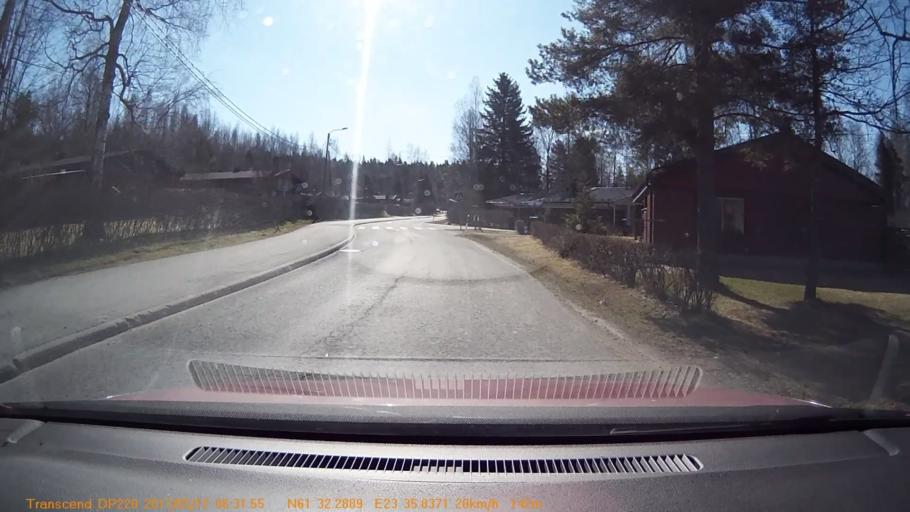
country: FI
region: Pirkanmaa
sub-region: Tampere
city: Yloejaervi
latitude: 61.5381
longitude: 23.5974
